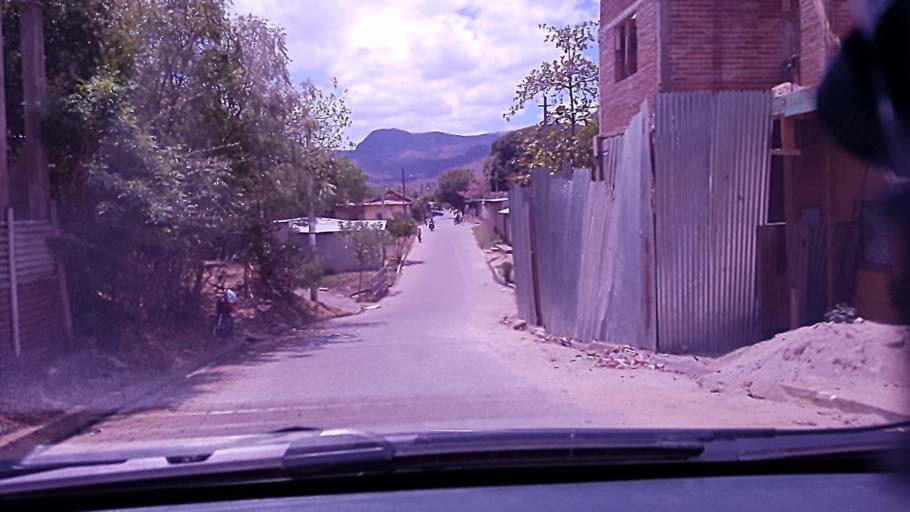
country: NI
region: Esteli
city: Condega
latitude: 13.3642
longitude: -86.3969
